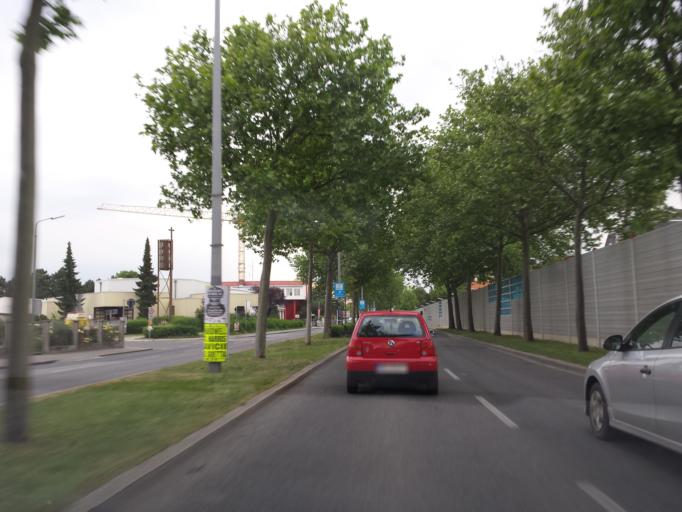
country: AT
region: Lower Austria
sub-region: Politischer Bezirk Wien-Umgebung
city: Gerasdorf bei Wien
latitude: 48.2259
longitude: 16.4639
